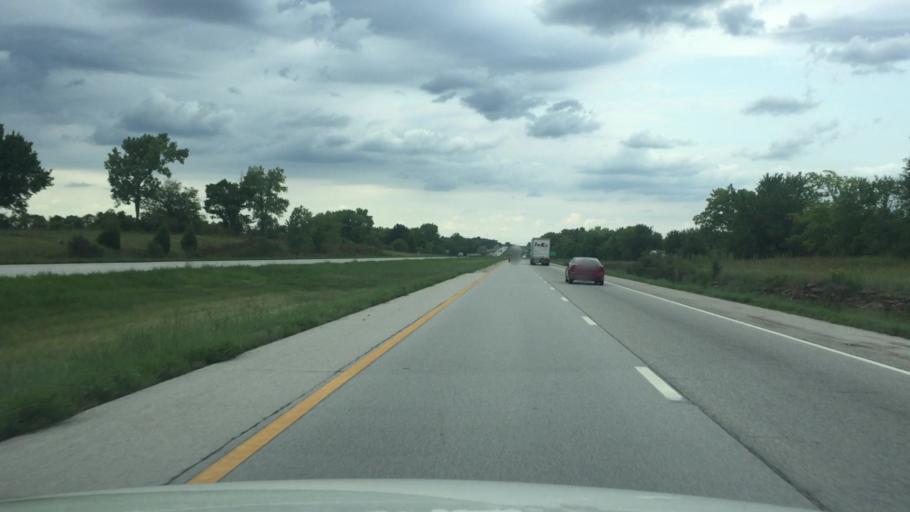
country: US
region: Kansas
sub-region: Miami County
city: Louisburg
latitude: 38.7541
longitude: -94.6774
